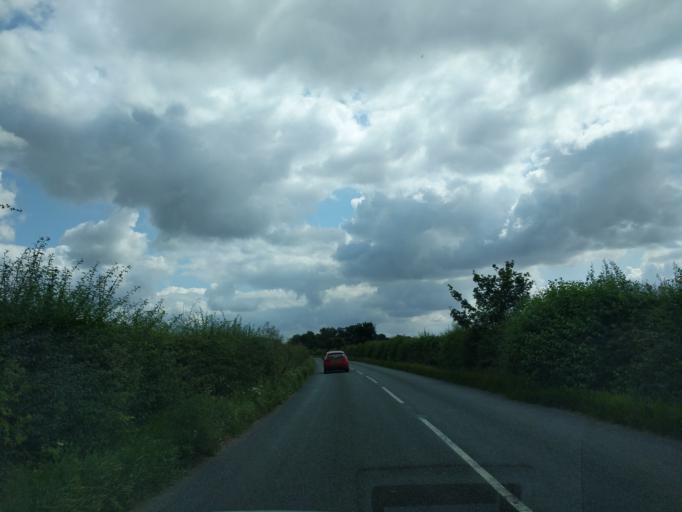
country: GB
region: England
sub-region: Cambridgeshire
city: Isleham
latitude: 52.2916
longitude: 0.4561
